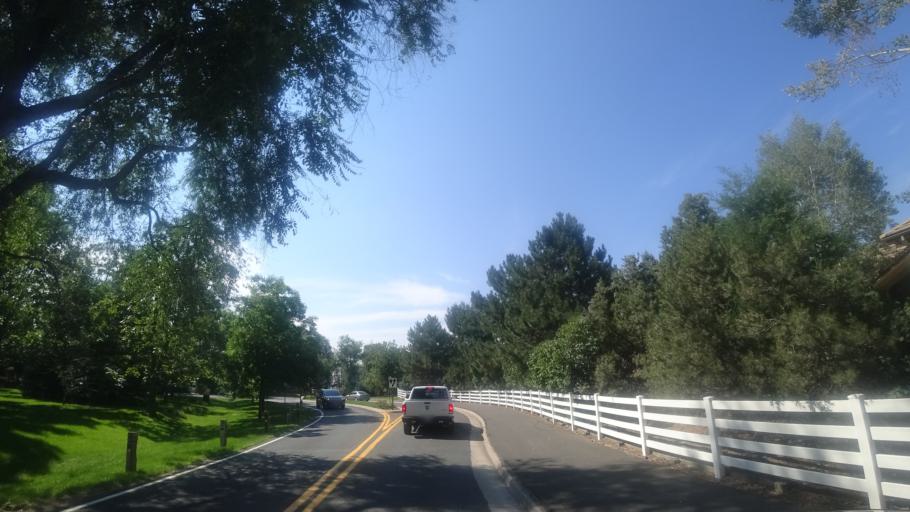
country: US
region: Colorado
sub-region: Arapahoe County
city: Englewood
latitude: 39.6388
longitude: -104.9777
